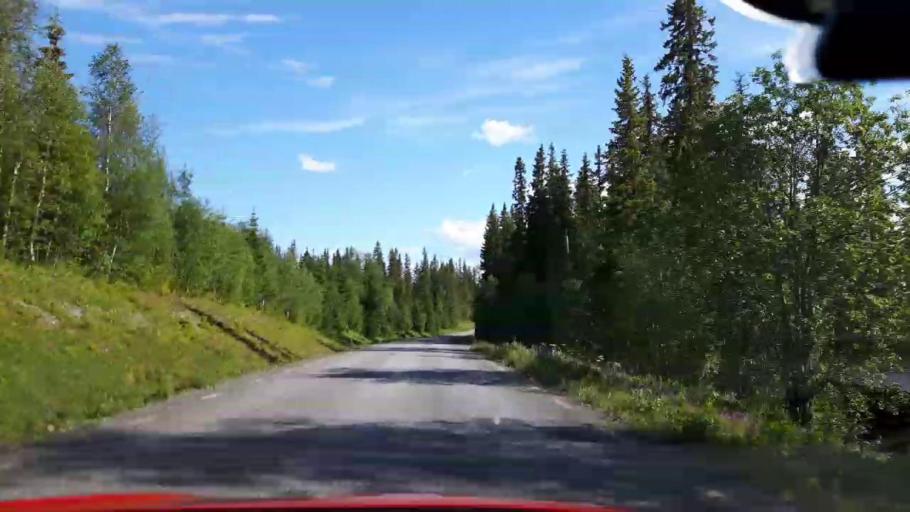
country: SE
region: Jaemtland
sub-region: Krokoms Kommun
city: Valla
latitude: 63.7146
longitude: 14.1356
